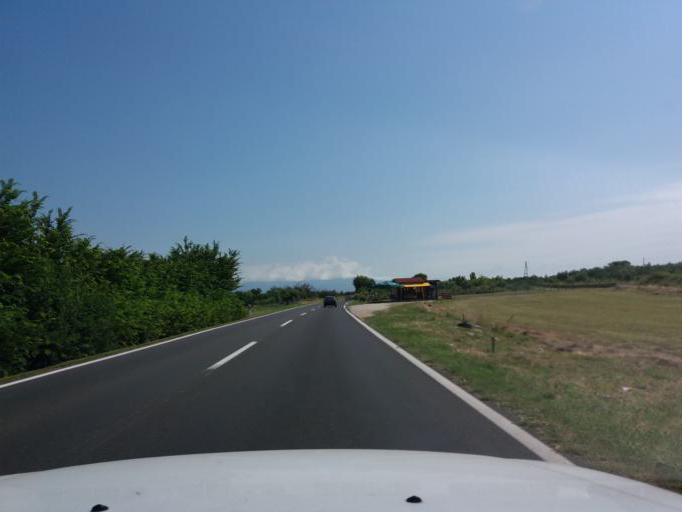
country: HR
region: Zadarska
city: Policnik
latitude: 44.1551
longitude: 15.3373
